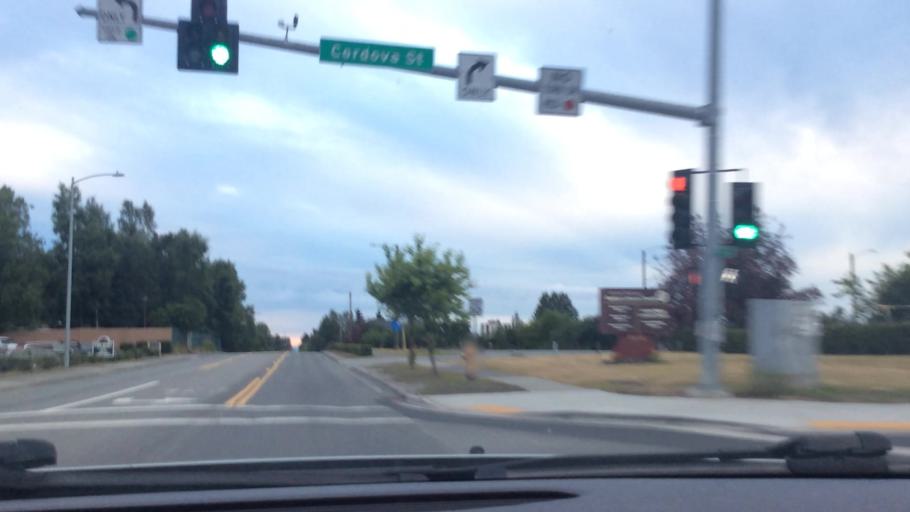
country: US
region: Alaska
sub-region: Anchorage Municipality
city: Anchorage
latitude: 61.2077
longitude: -149.8791
